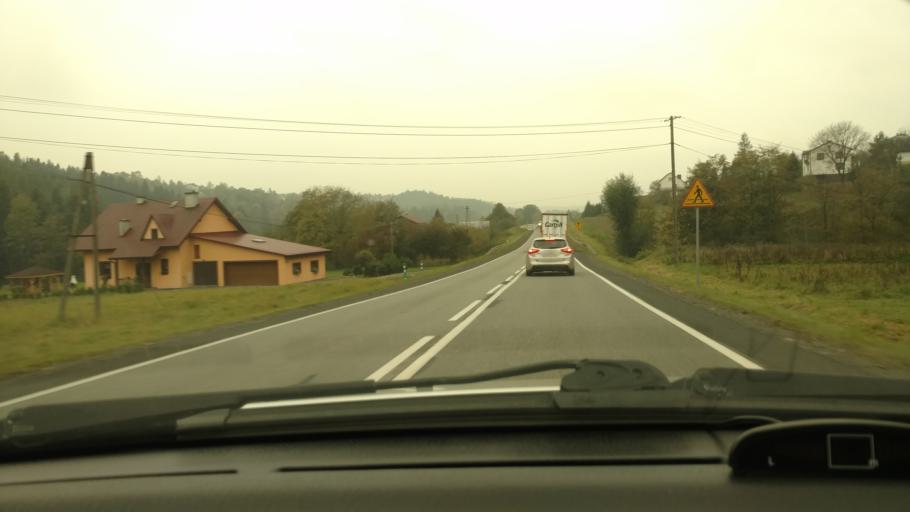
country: PL
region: Lesser Poland Voivodeship
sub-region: Powiat nowosadecki
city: Kamionka Wielka
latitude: 49.6148
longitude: 20.8166
